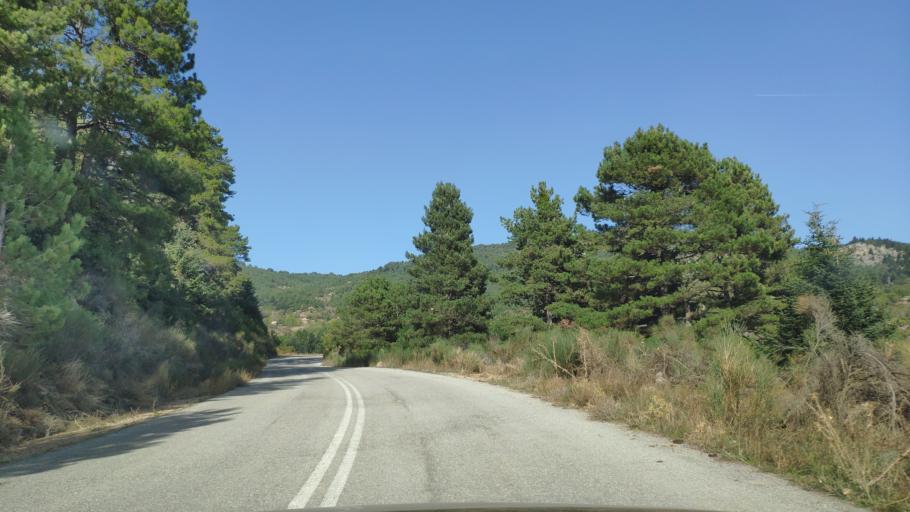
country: GR
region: West Greece
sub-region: Nomos Achaias
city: Aiyira
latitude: 38.0124
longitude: 22.4039
